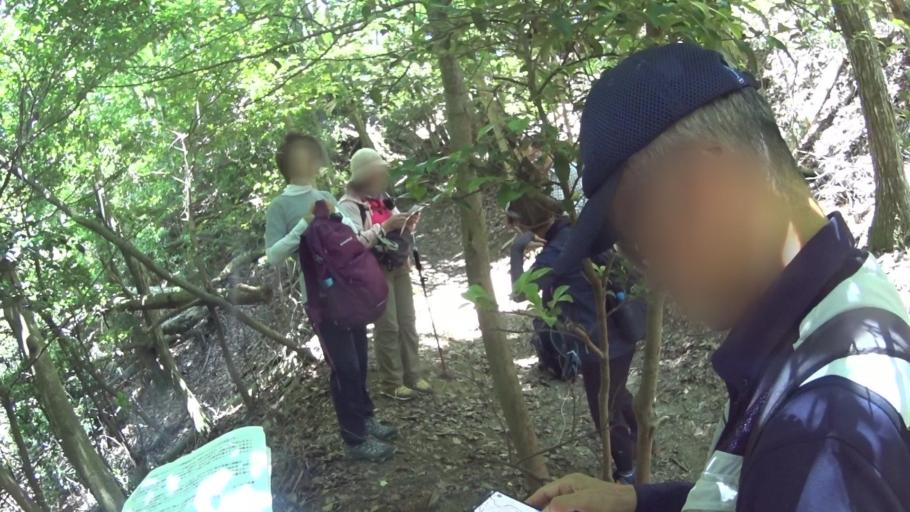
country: JP
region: Kyoto
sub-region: Kyoto-shi
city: Kamigyo-ku
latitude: 35.0487
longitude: 135.8129
